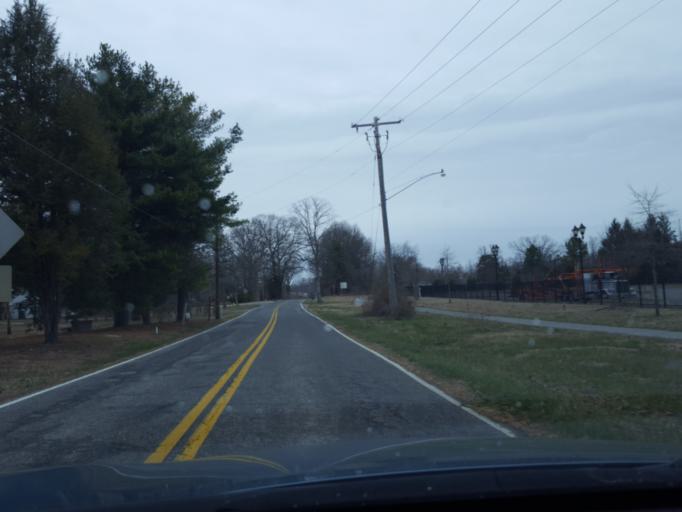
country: US
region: Maryland
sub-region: Calvert County
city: Prince Frederick
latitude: 38.5475
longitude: -76.5828
